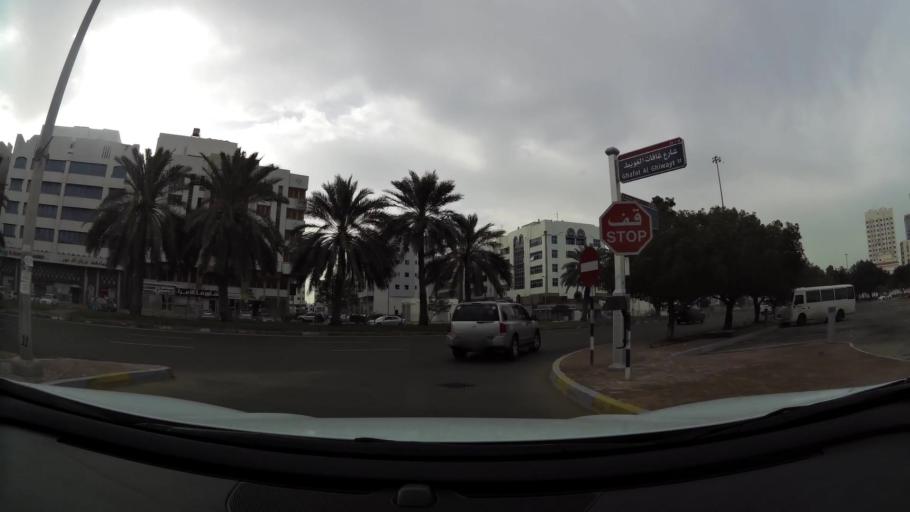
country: AE
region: Abu Dhabi
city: Abu Dhabi
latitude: 24.4657
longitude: 54.3803
